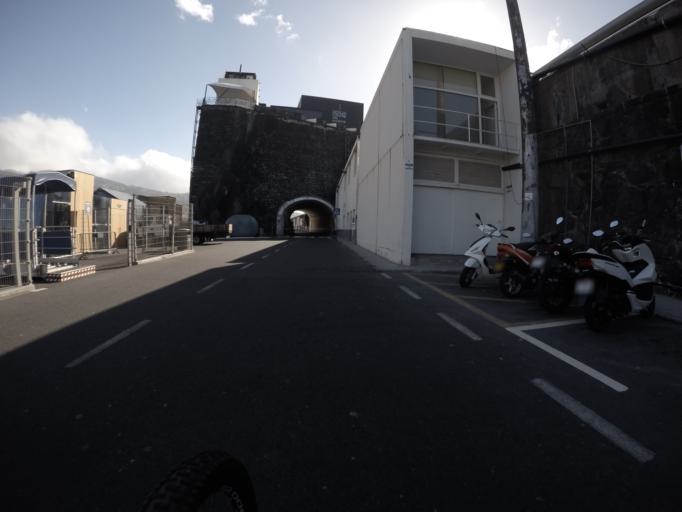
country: PT
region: Madeira
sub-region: Funchal
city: Funchal
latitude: 32.6411
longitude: -16.9157
